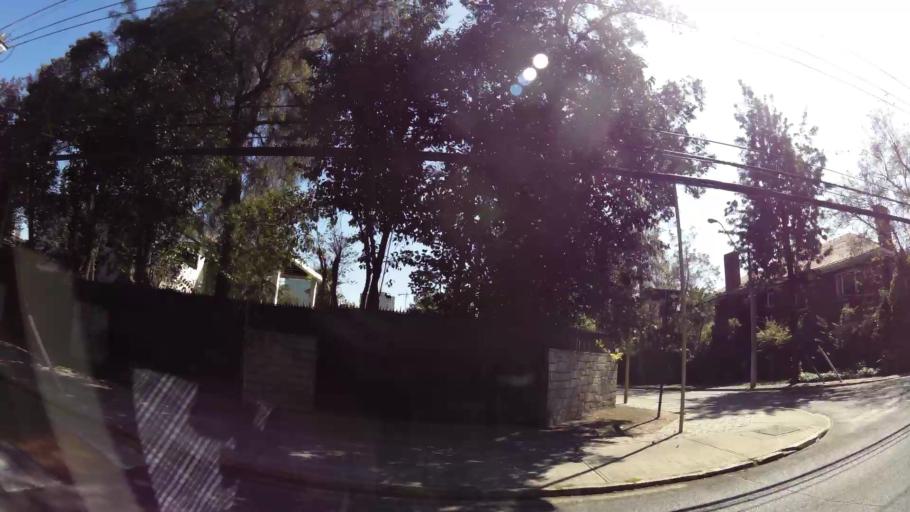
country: CL
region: Santiago Metropolitan
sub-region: Provincia de Santiago
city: Villa Presidente Frei, Nunoa, Santiago, Chile
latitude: -33.4172
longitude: -70.5798
